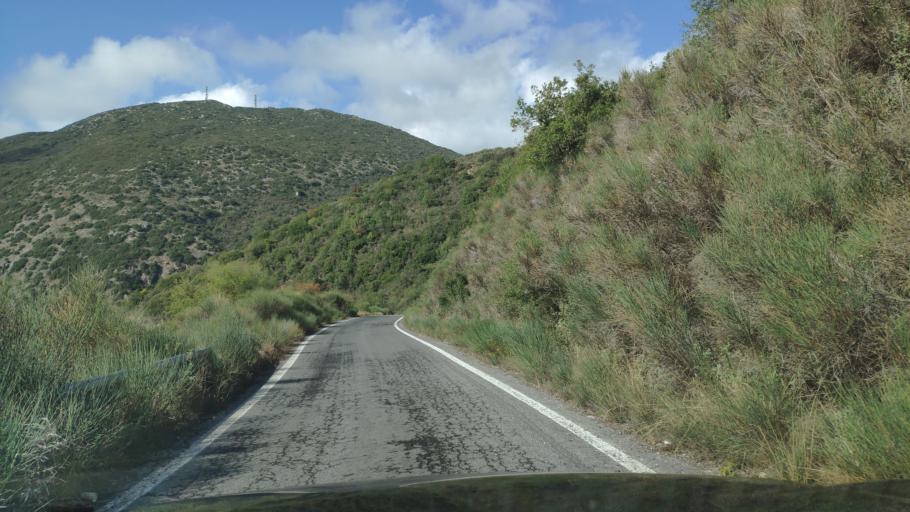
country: GR
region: Peloponnese
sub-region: Nomos Arkadias
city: Dimitsana
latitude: 37.5703
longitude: 22.0202
